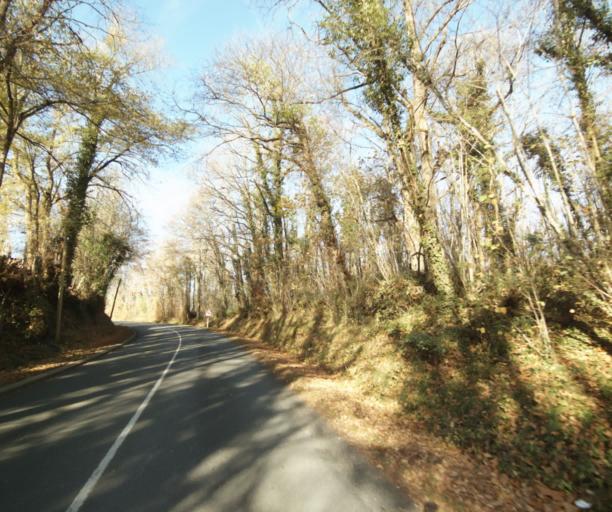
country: FR
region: Poitou-Charentes
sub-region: Departement de la Charente-Maritime
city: Ecoyeux
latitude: 45.7656
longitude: -0.4968
